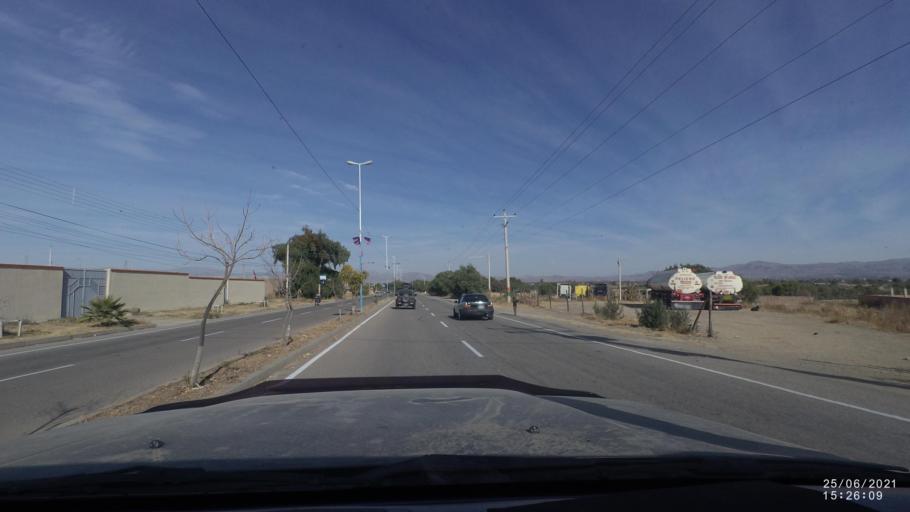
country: BO
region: Cochabamba
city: Cliza
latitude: -17.5360
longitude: -65.9617
